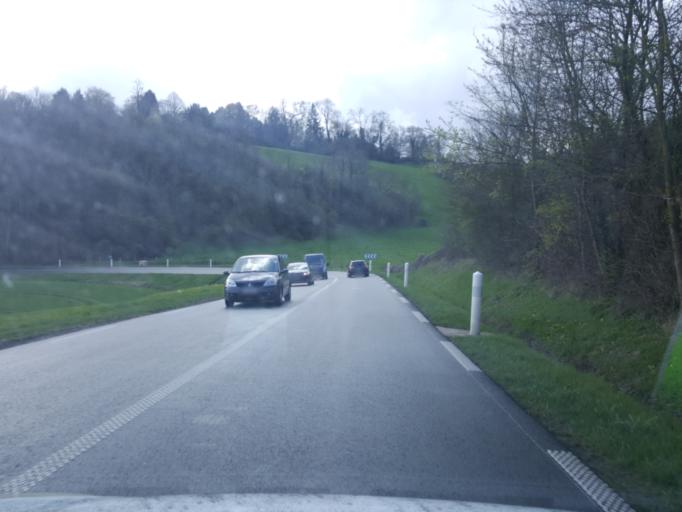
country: FR
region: Picardie
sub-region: Departement de l'Oise
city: Auneuil
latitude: 49.3671
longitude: 1.9794
